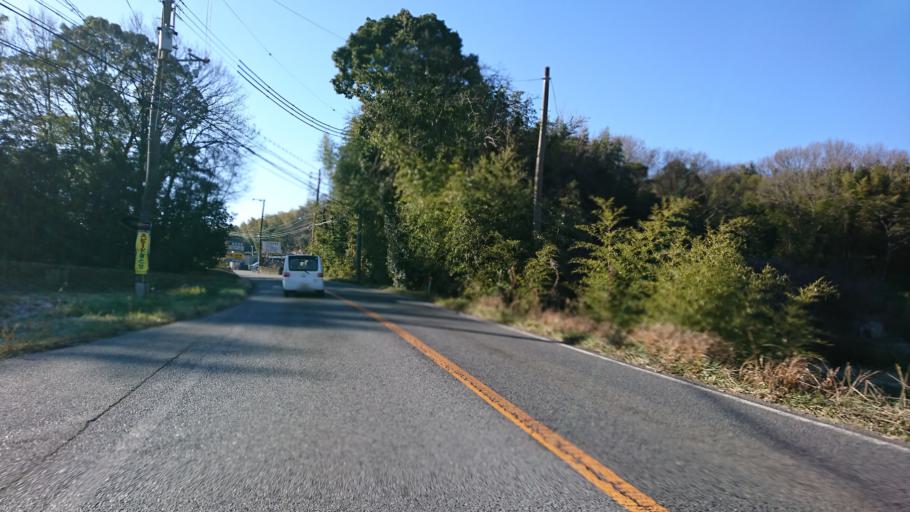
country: JP
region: Hyogo
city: Kakogawacho-honmachi
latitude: 34.8227
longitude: 134.8350
